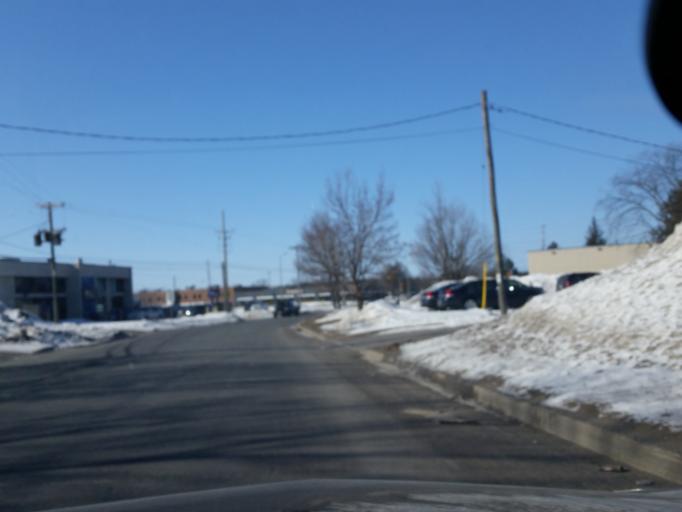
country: CA
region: Ontario
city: Ottawa
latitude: 45.3323
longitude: -75.7206
